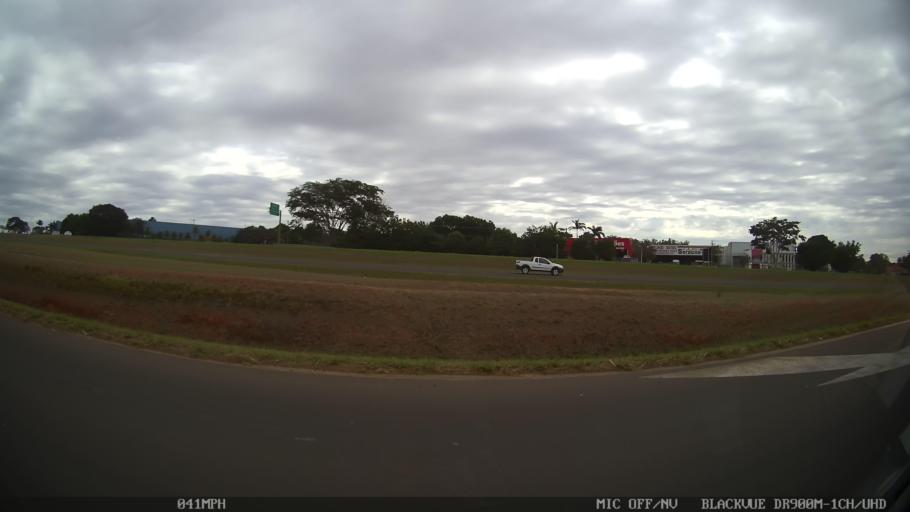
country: BR
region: Sao Paulo
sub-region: Bady Bassitt
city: Bady Bassitt
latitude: -20.8060
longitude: -49.5202
